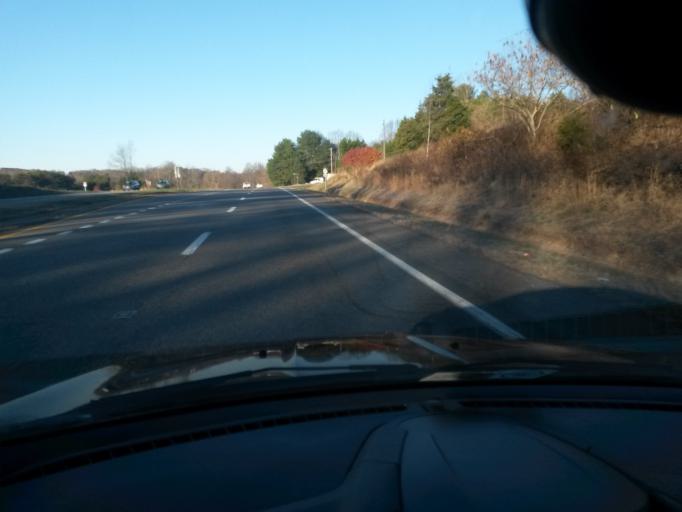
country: US
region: Virginia
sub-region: Henry County
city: Horse Pasture
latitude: 36.6227
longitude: -79.9917
